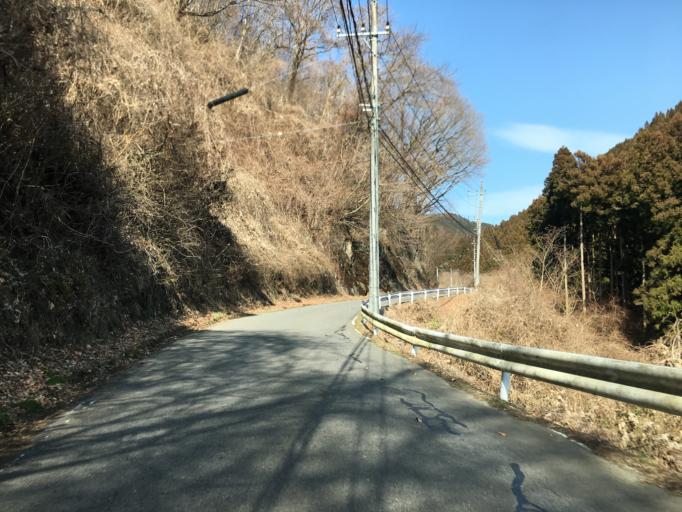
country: JP
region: Ibaraki
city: Daigo
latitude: 36.8044
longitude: 140.4968
